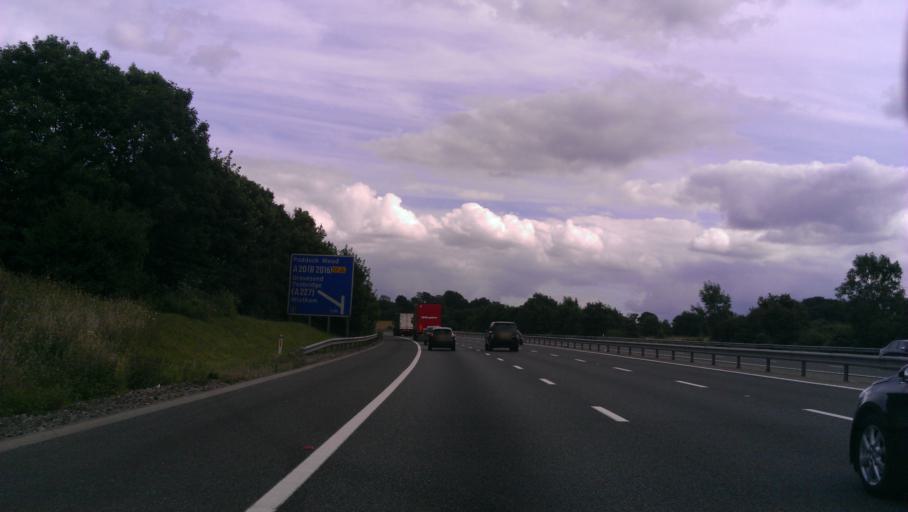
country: GB
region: England
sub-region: Kent
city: Borough Green
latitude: 51.3232
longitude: 0.2767
